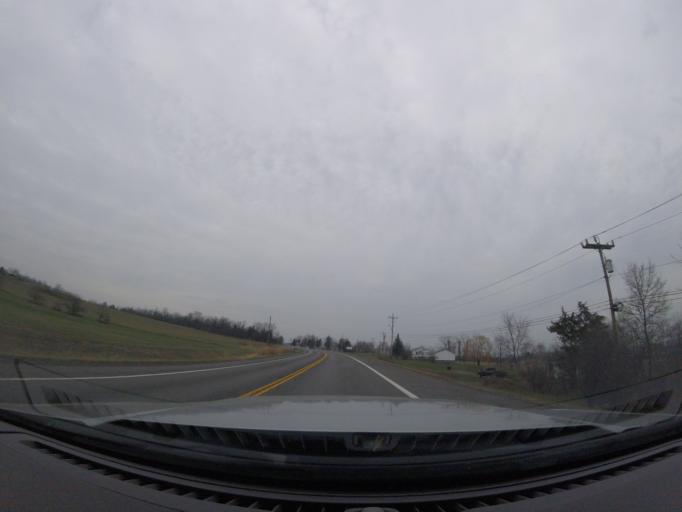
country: US
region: New York
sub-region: Yates County
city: Penn Yan
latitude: 42.6721
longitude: -76.9483
